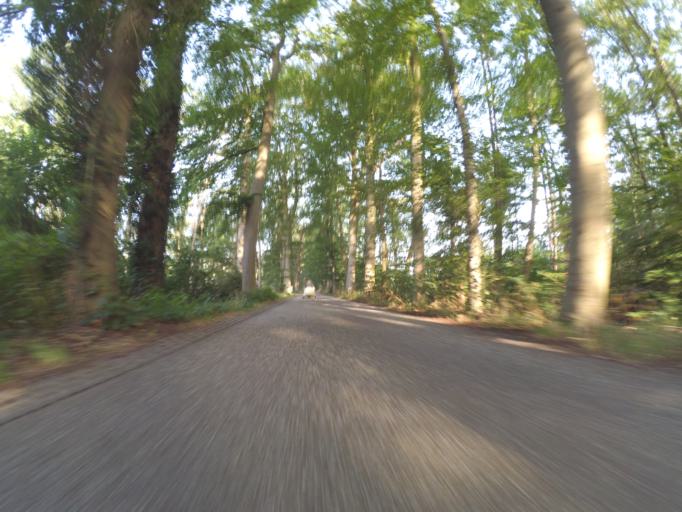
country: NL
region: Overijssel
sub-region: Gemeente Wierden
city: Wierden
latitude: 52.3290
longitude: 6.5391
